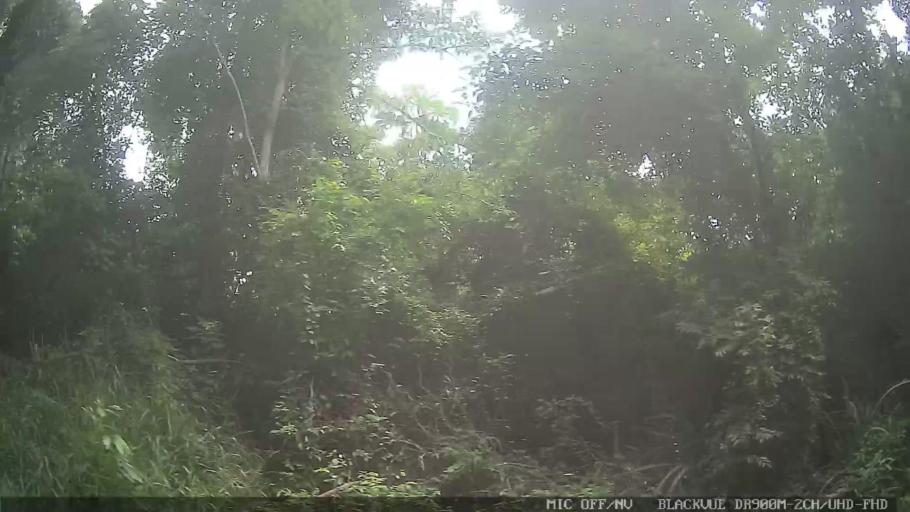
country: BR
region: Minas Gerais
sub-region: Extrema
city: Extrema
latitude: -22.8768
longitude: -46.3242
